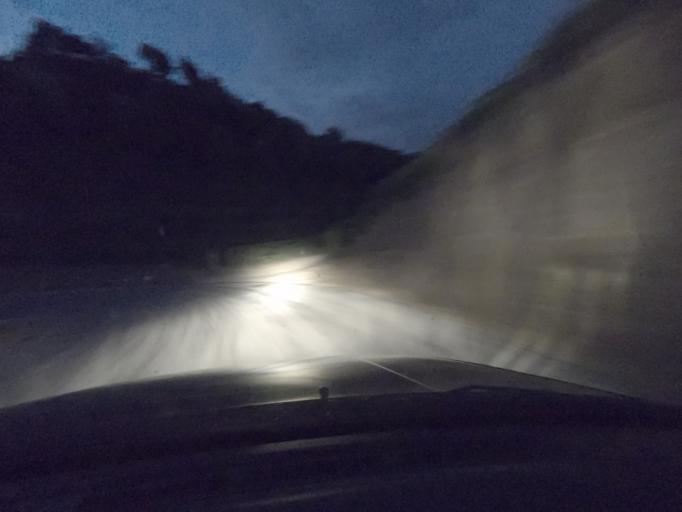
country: PT
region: Vila Real
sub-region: Peso da Regua
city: Godim
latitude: 41.1875
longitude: -7.8358
